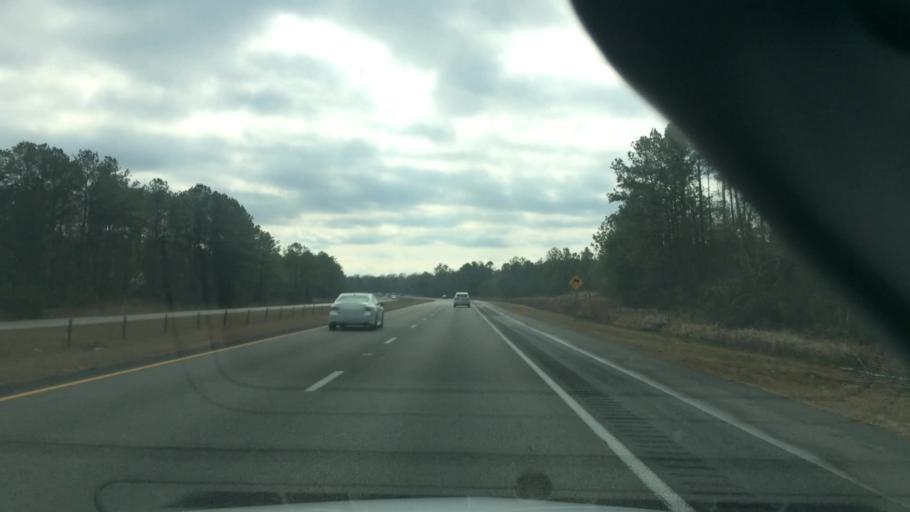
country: US
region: North Carolina
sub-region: New Hanover County
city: Castle Hayne
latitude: 34.3751
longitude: -77.8849
